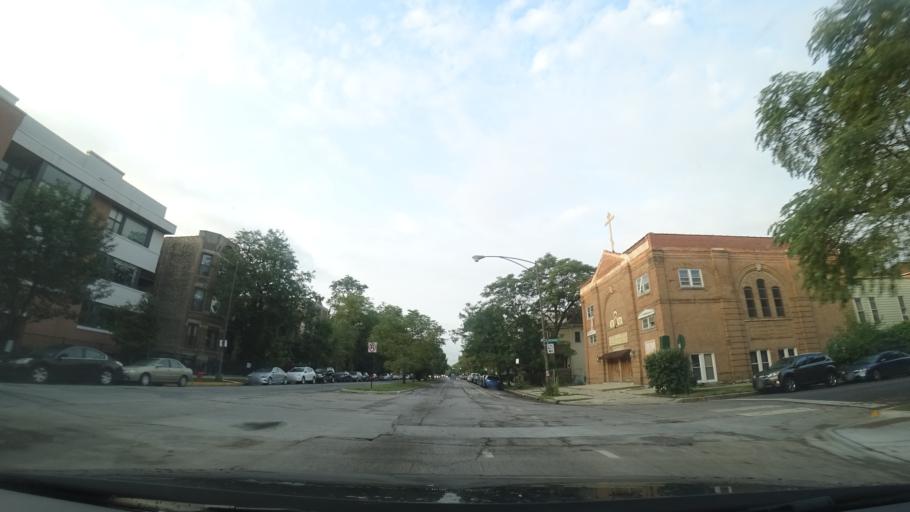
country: US
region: Illinois
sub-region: Cook County
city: Oak Park
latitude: 41.9194
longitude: -87.7071
